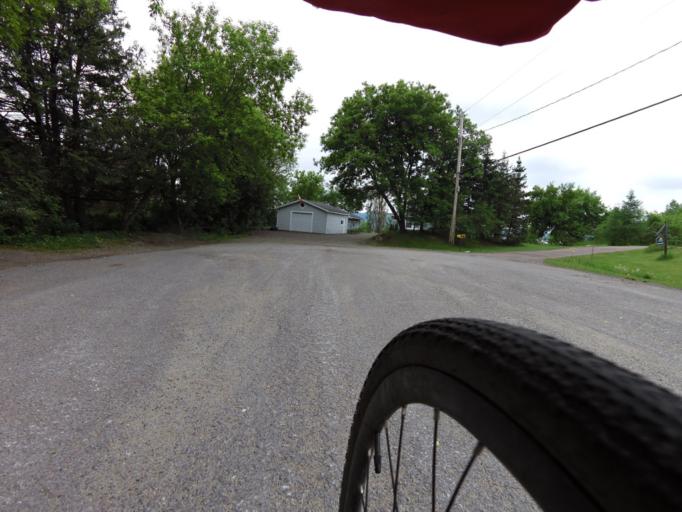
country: CA
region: Ontario
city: Renfrew
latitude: 45.2910
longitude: -76.7240
